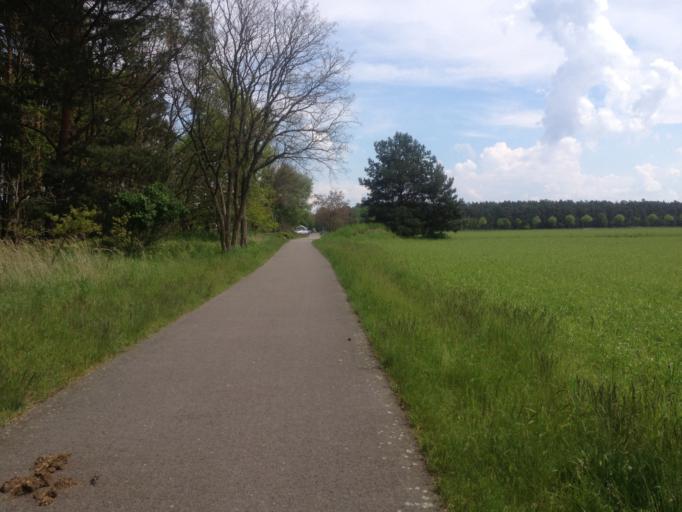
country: DE
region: Brandenburg
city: Briesen
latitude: 51.8081
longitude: 14.2429
